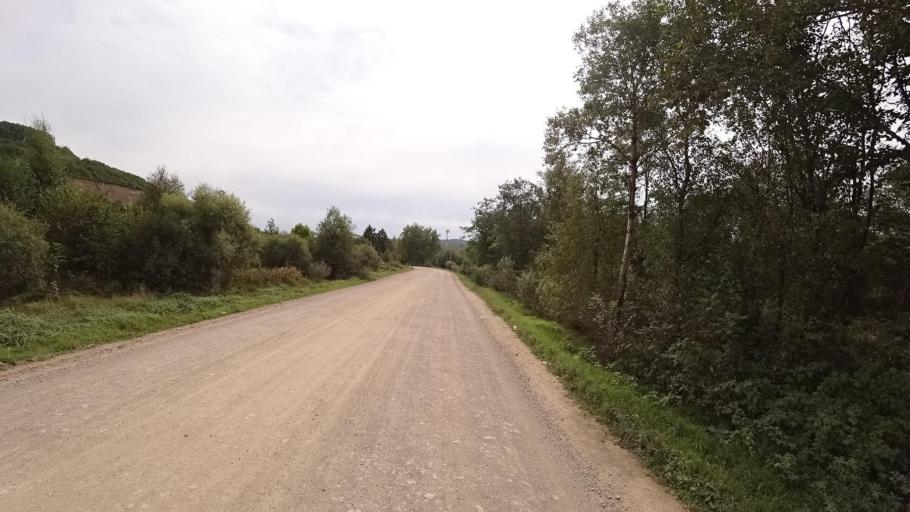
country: RU
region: Jewish Autonomous Oblast
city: Khingansk
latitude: 48.9915
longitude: 131.0524
